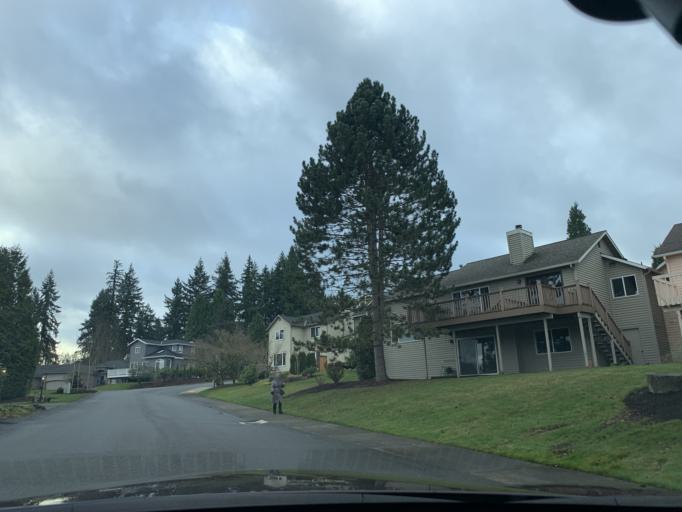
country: US
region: Washington
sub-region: King County
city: Woodinville
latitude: 47.7347
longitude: -122.1581
